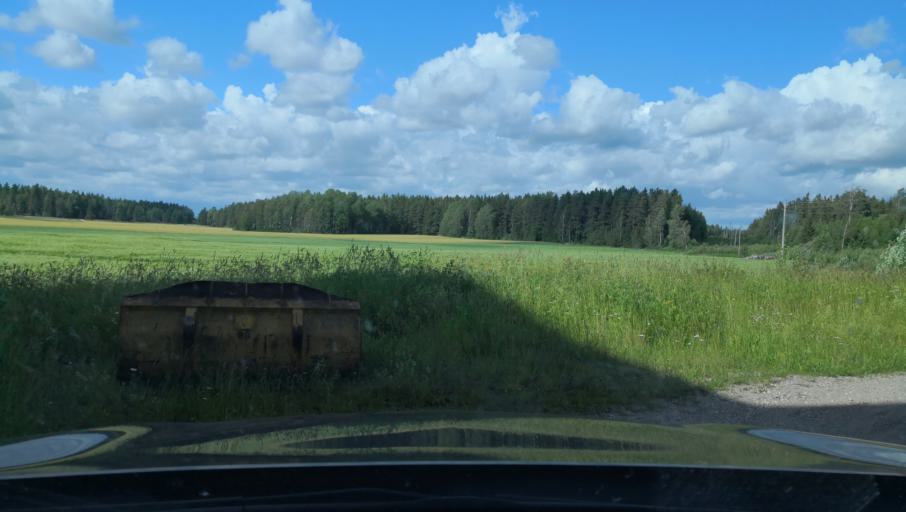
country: SE
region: Vaestmanland
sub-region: Kungsors Kommun
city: Kungsoer
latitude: 59.3220
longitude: 16.0703
